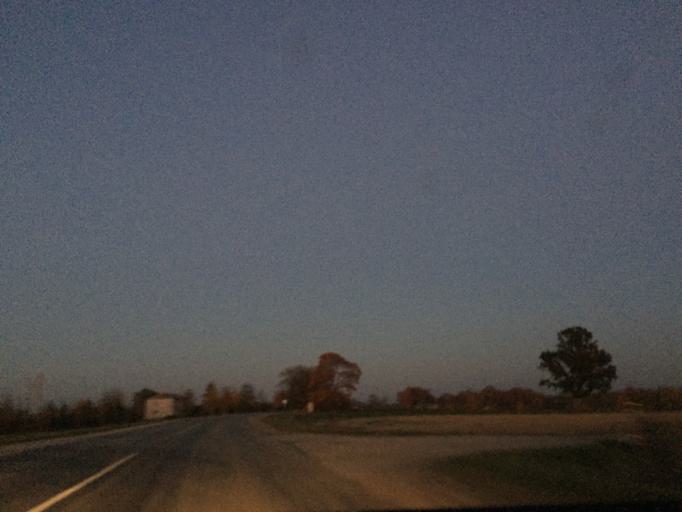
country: LV
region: Tervete
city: Zelmeni
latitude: 56.5029
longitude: 23.2665
